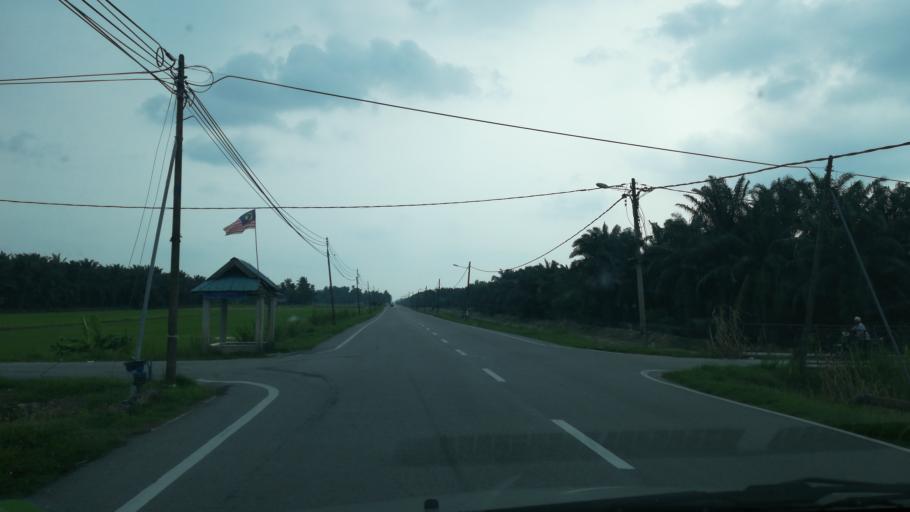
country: MY
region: Perak
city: Teluk Intan
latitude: 4.1196
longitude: 101.0780
